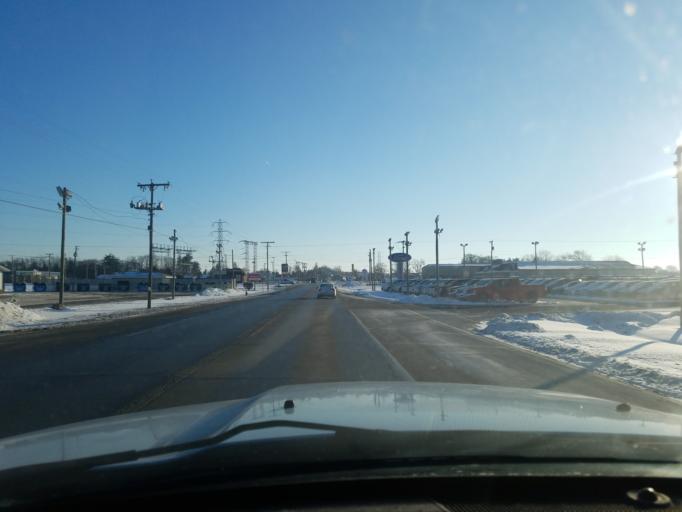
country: US
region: Indiana
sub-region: Noble County
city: Ligonier
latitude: 41.4521
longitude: -85.5924
